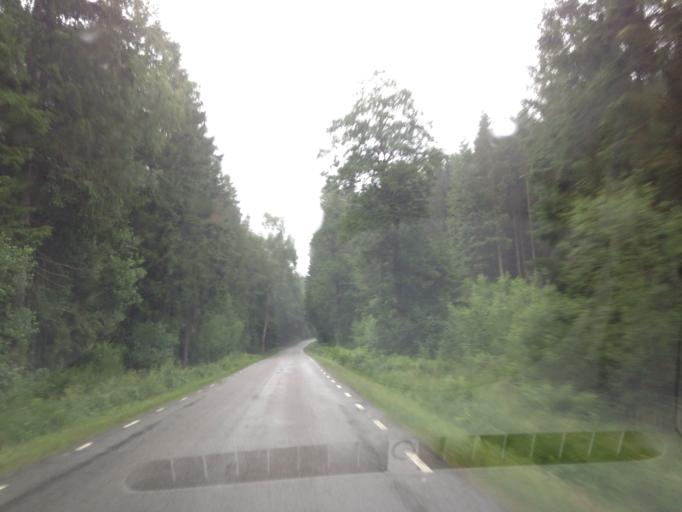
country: SE
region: Vaestra Goetaland
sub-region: Marks Kommun
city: Horred
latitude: 57.1637
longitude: 12.7015
